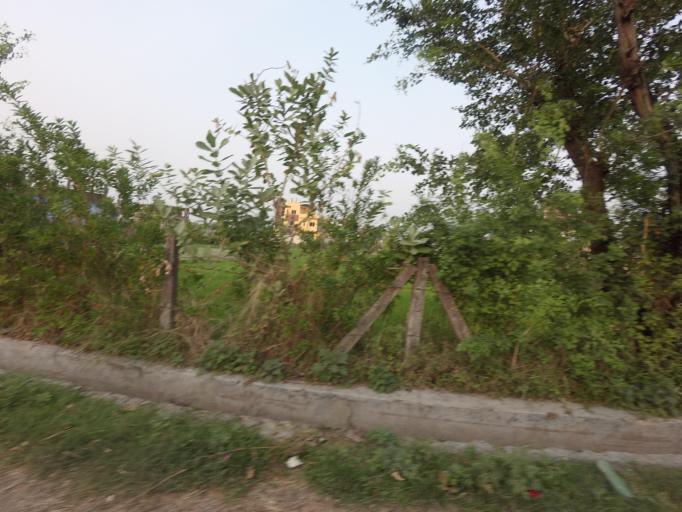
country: NP
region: Western Region
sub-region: Lumbini Zone
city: Bhairahawa
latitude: 27.5161
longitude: 83.4577
